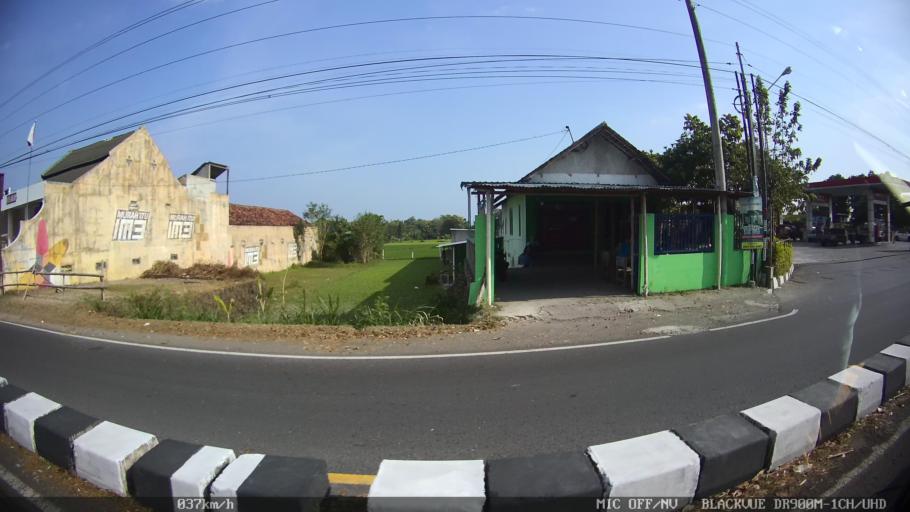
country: ID
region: Daerah Istimewa Yogyakarta
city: Sewon
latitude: -7.8382
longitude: 110.4001
